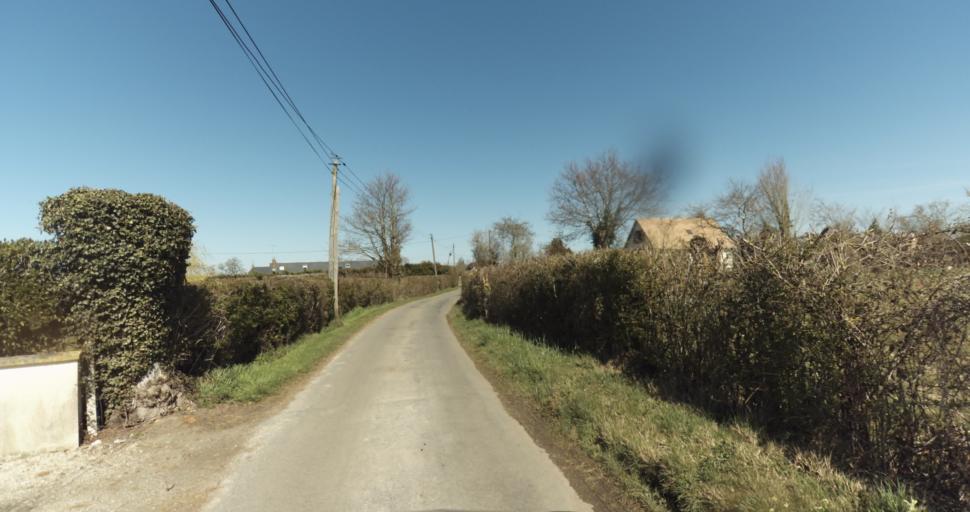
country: FR
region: Lower Normandy
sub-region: Departement du Calvados
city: Livarot
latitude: 48.9952
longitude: 0.1039
